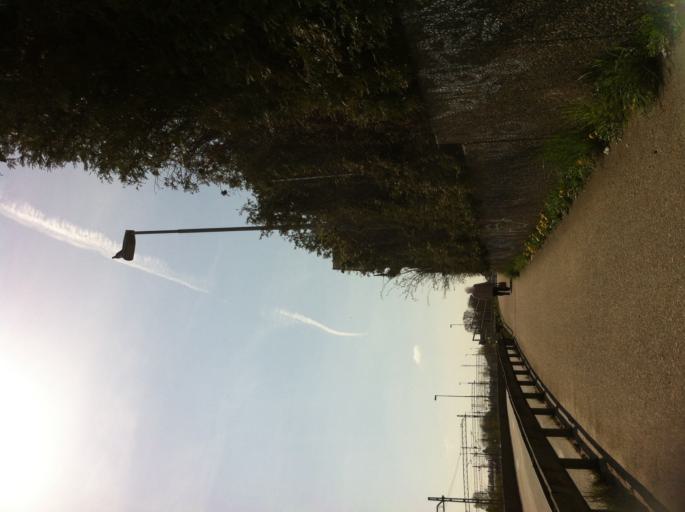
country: SE
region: Skane
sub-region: Kavlinge Kommun
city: Kaevlinge
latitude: 55.7974
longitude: 13.1103
